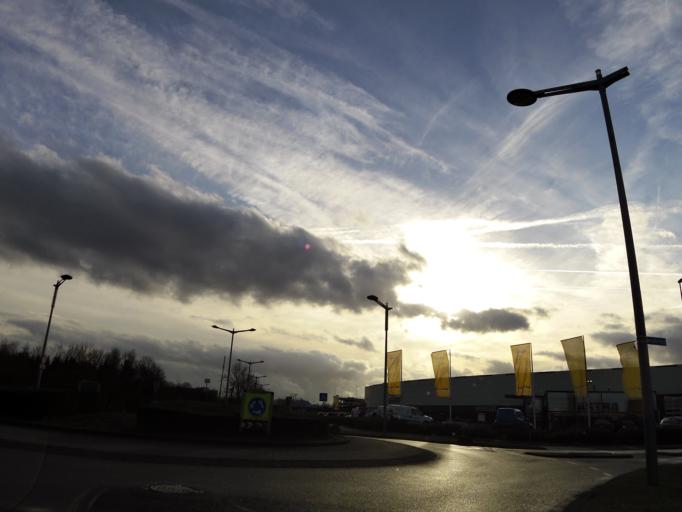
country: NL
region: Limburg
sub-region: Gemeente Heerlen
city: Nieuw-Lotbroek
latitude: 50.9028
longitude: 5.9481
